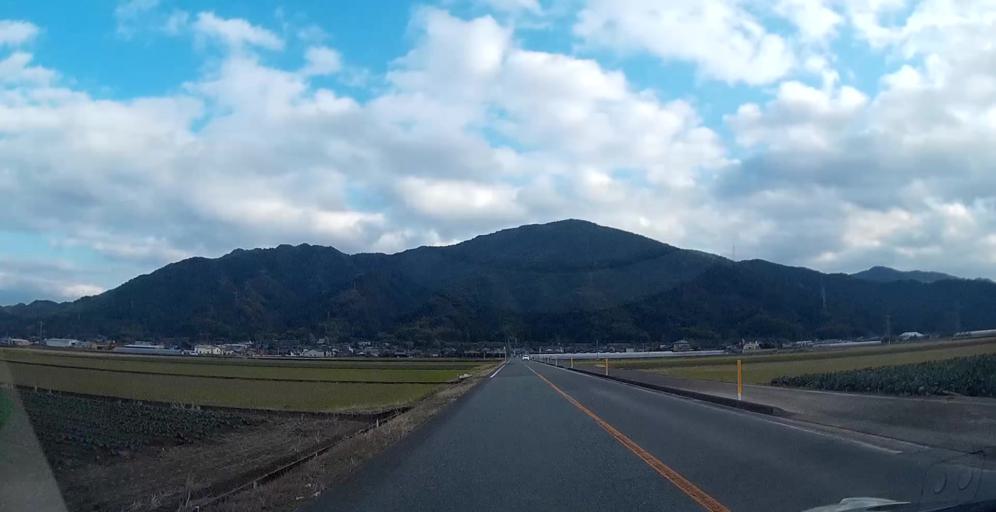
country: JP
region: Kumamoto
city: Yatsushiro
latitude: 32.5311
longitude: 130.6547
